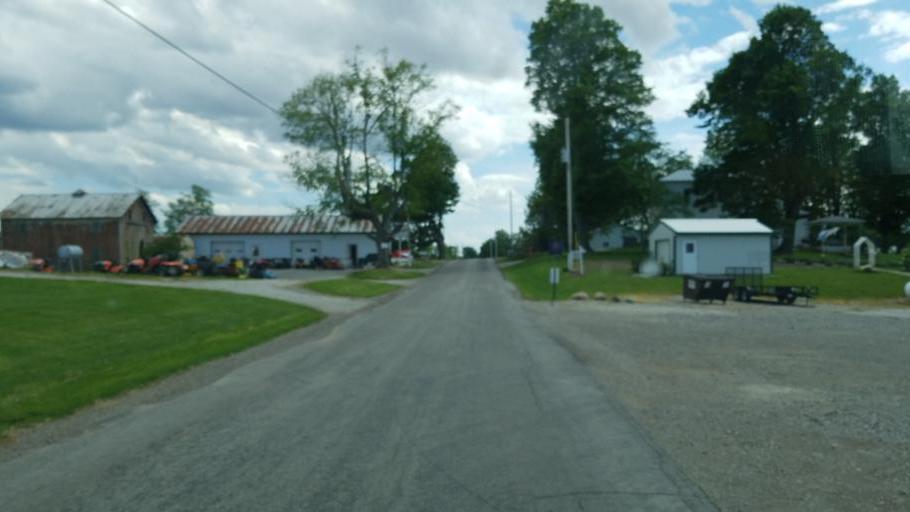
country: US
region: Ohio
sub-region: Huron County
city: Plymouth
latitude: 40.9797
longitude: -82.6062
